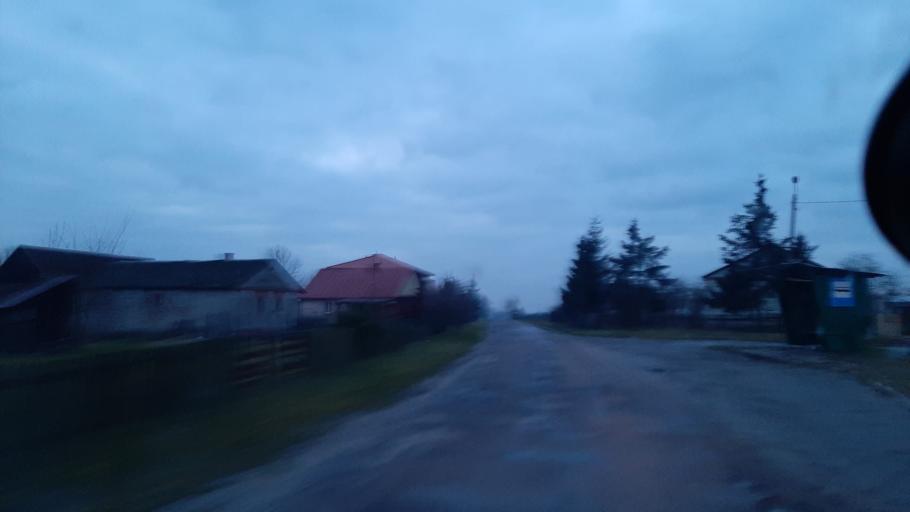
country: PL
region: Lublin Voivodeship
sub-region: Powiat lubartowski
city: Firlej
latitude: 51.6016
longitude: 22.5126
